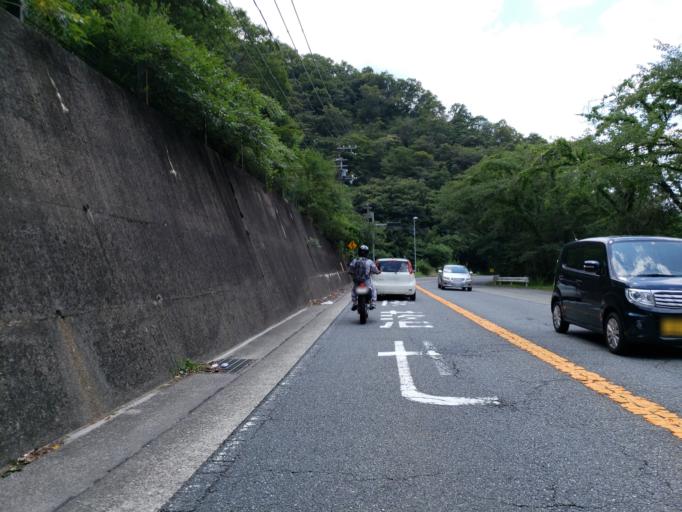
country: JP
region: Hyogo
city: Aioi
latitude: 34.7864
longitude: 134.4404
